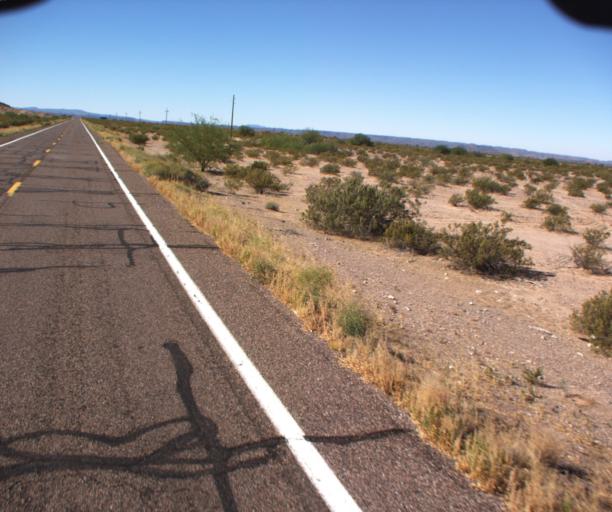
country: US
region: Arizona
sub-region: Maricopa County
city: Gila Bend
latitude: 32.7001
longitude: -112.8489
